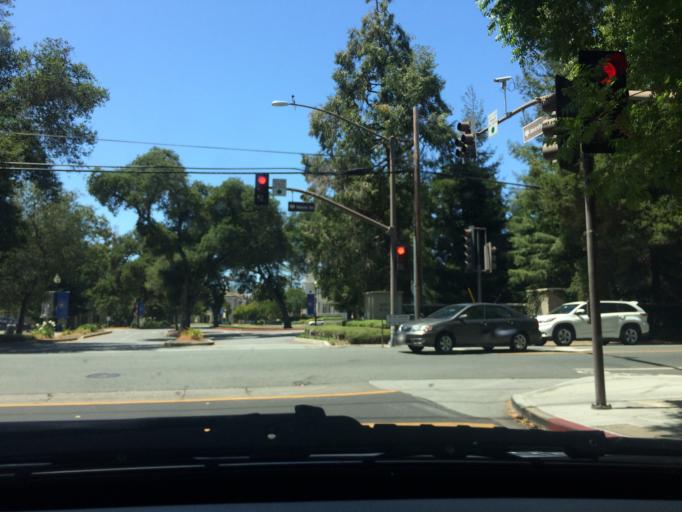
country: US
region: California
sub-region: San Mateo County
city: Menlo Park
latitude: 37.4523
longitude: -122.1903
